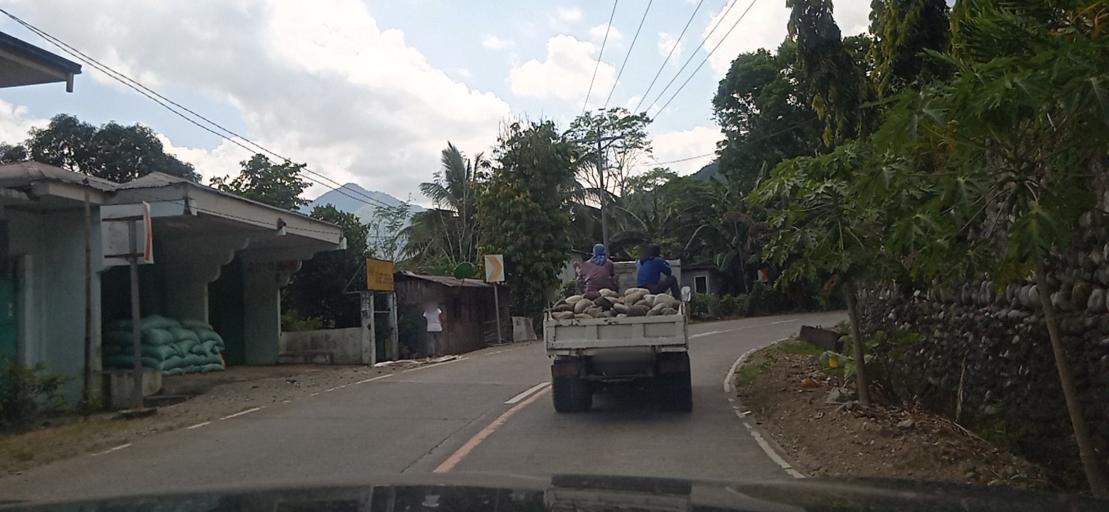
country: PH
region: Cordillera
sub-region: Kalinga
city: Balbalan
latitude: 17.4042
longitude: 121.3172
